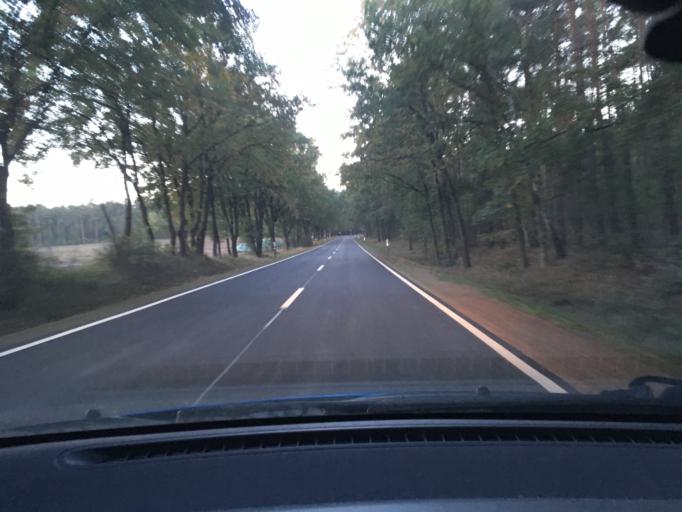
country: DE
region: Lower Saxony
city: Neetze
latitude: 53.2567
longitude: 10.6107
